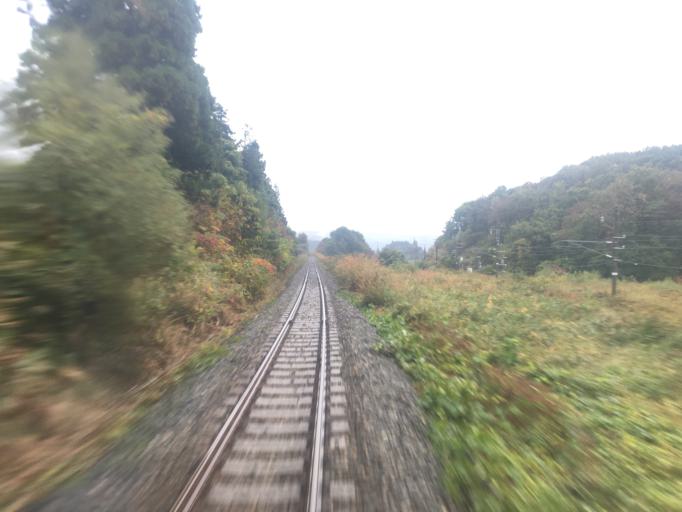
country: JP
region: Yamagata
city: Shinjo
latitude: 38.7130
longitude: 140.3140
